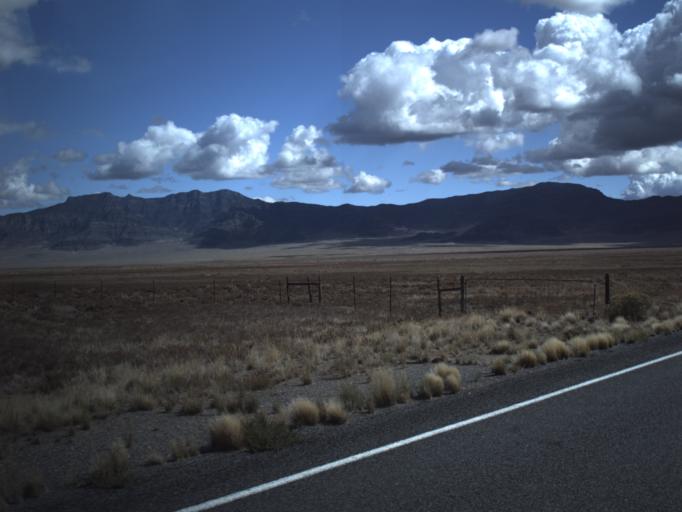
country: US
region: Utah
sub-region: Beaver County
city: Milford
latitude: 38.5503
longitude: -113.7306
